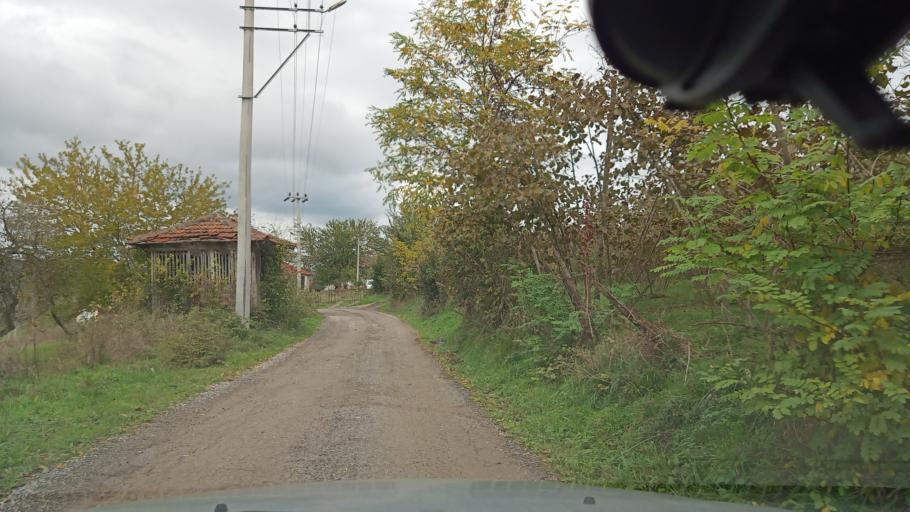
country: TR
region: Sakarya
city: Karasu
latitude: 41.0891
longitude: 30.5864
